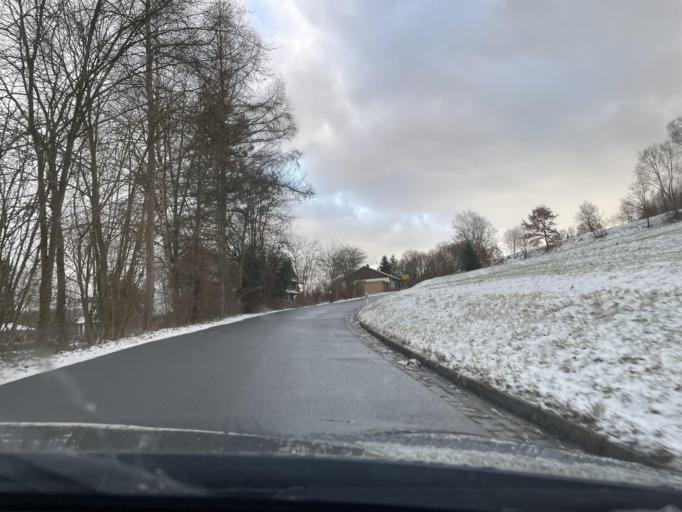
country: DE
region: Bavaria
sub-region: Lower Bavaria
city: Viechtach
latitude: 49.0902
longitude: 12.8774
